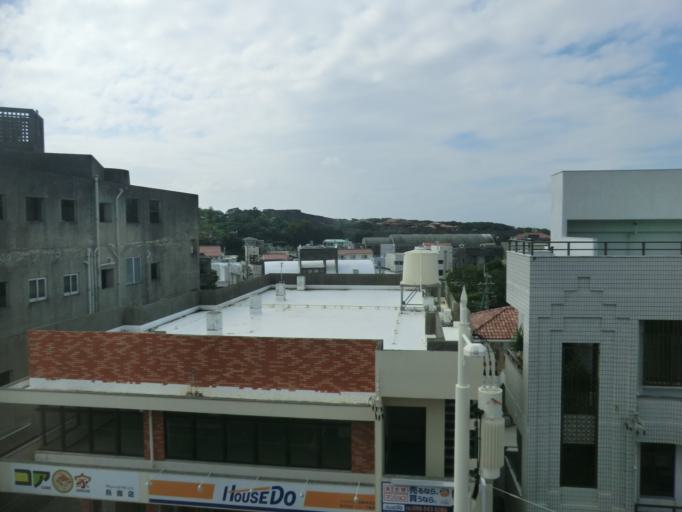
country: JP
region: Okinawa
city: Naha-shi
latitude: 26.2197
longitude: 127.7231
